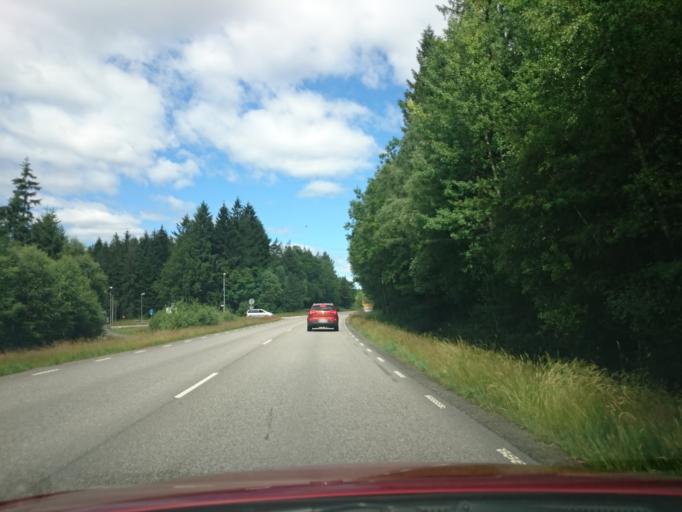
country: SE
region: Vaestra Goetaland
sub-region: Lerums Kommun
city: Grabo
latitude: 57.8248
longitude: 12.2933
